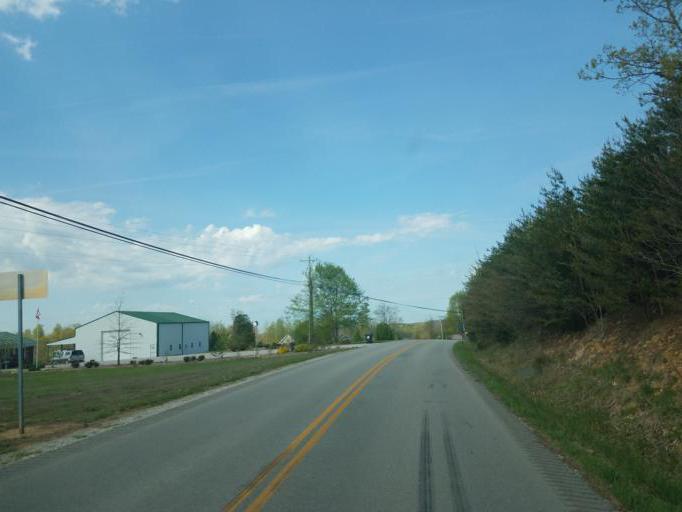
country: US
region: Kentucky
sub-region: Edmonson County
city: Brownsville
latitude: 37.2703
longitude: -86.2034
